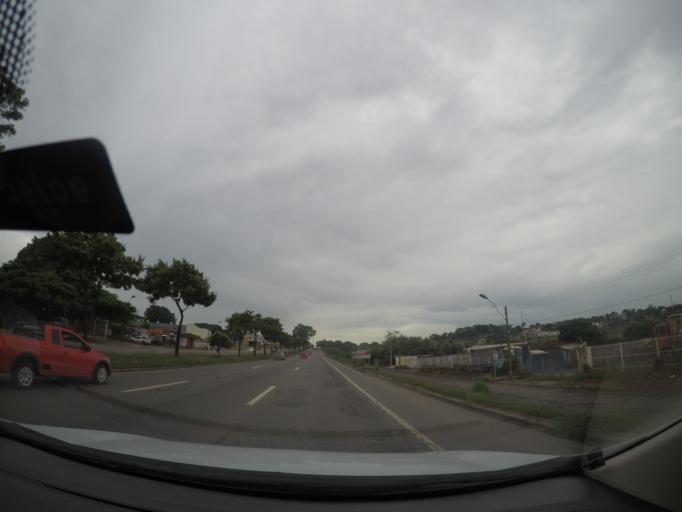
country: BR
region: Goias
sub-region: Goiania
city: Goiania
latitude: -16.6395
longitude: -49.2850
